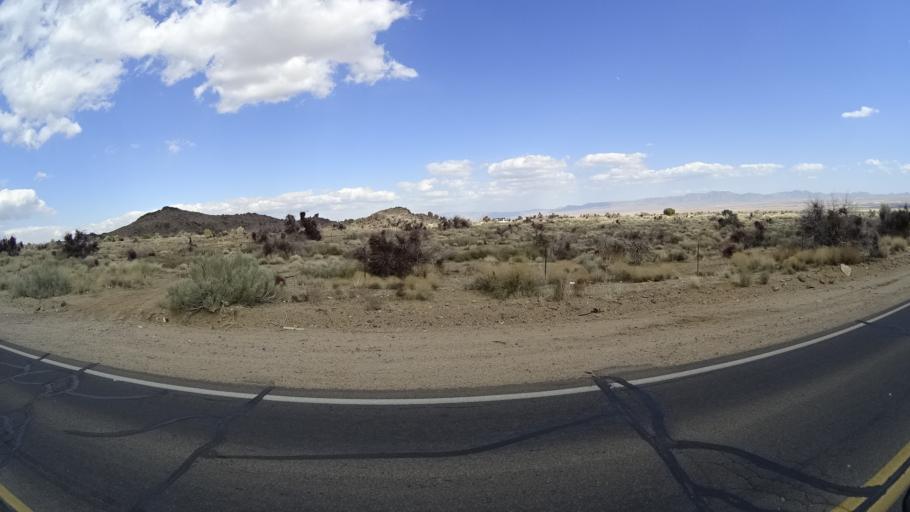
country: US
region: Arizona
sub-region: Mohave County
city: New Kingman-Butler
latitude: 35.2872
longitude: -114.0572
